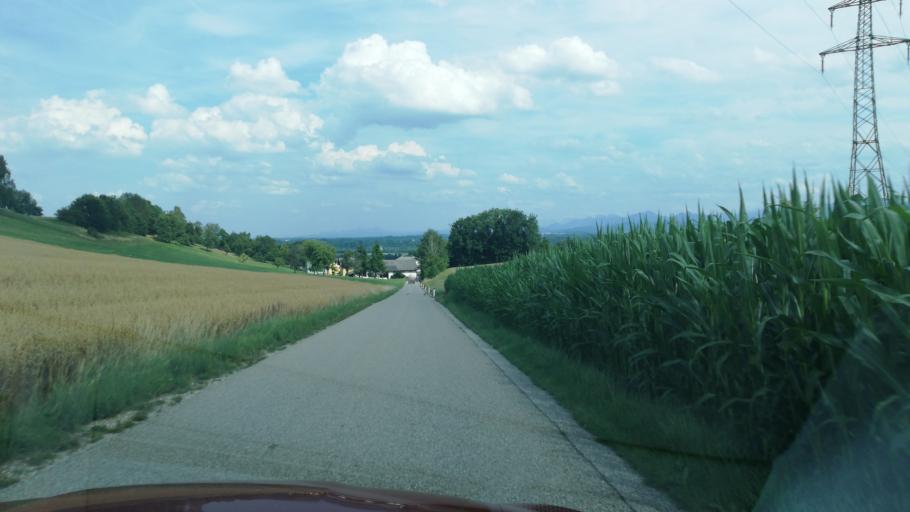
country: AT
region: Upper Austria
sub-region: Politischer Bezirk Vocklabruck
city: Puhret
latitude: 48.0363
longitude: 13.7189
